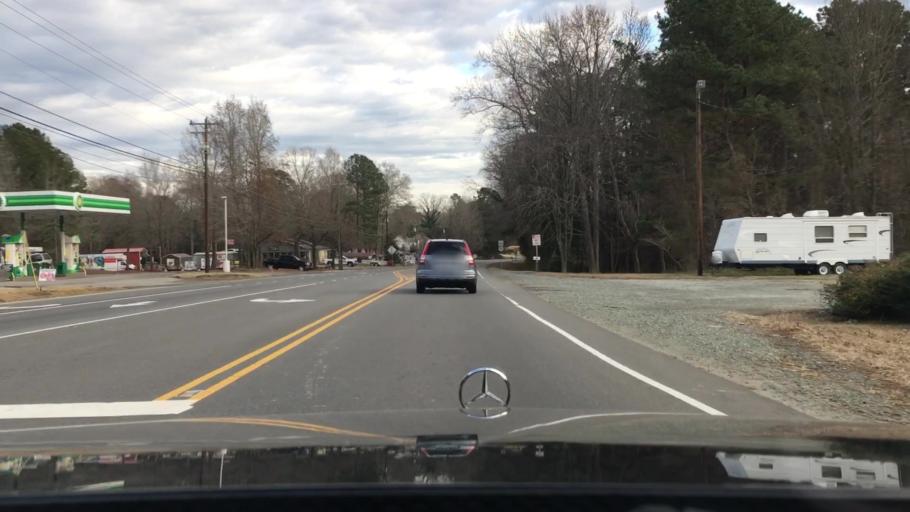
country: US
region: North Carolina
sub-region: Orange County
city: Hillsborough
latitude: 36.0819
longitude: -79.0795
